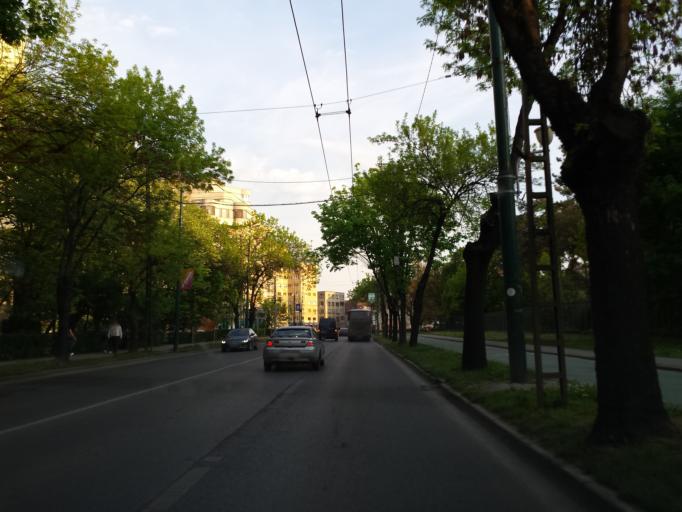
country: RO
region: Timis
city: Timisoara
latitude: 45.7609
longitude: 21.2271
